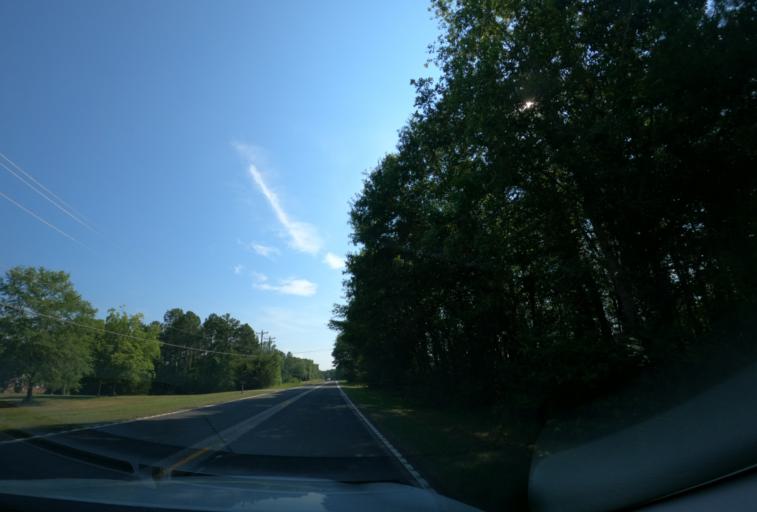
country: US
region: South Carolina
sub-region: Anderson County
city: Belton
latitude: 34.4569
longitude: -82.5447
